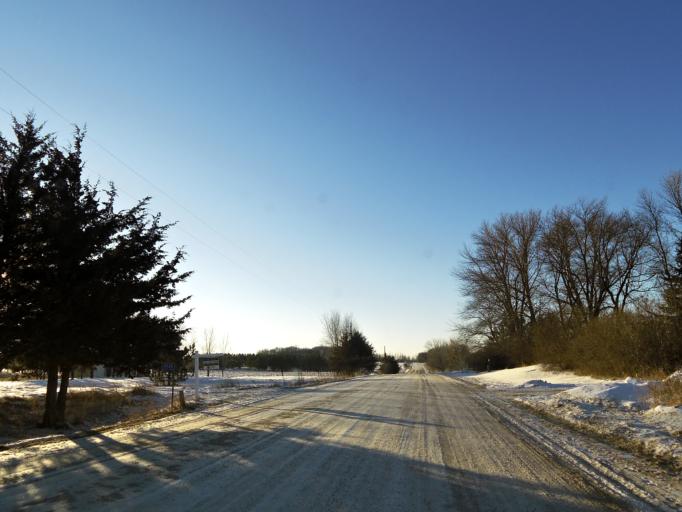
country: US
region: Minnesota
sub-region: Scott County
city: Jordan
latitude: 44.6519
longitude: -93.5163
